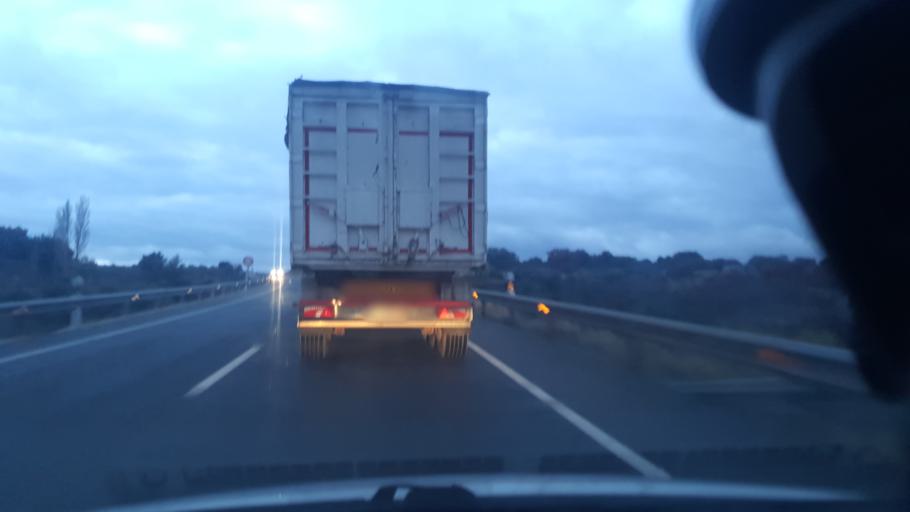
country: ES
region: Castille and Leon
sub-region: Provincia de Avila
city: Mediana de Voltoya
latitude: 40.7183
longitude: -4.5435
